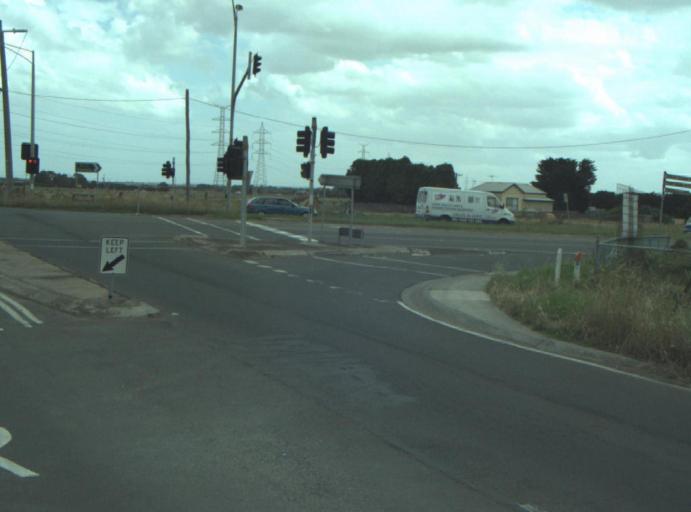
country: AU
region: Victoria
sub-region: Greater Geelong
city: Leopold
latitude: -38.1780
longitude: 144.4204
